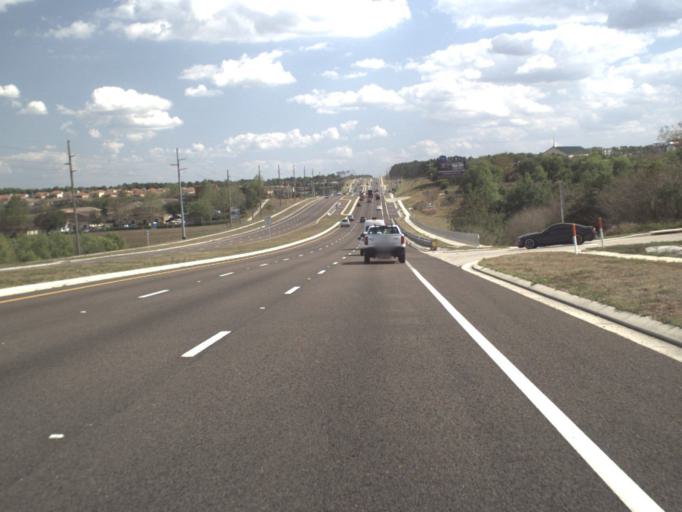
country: US
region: Florida
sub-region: Lake County
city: Clermont
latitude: 28.5253
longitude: -81.7315
